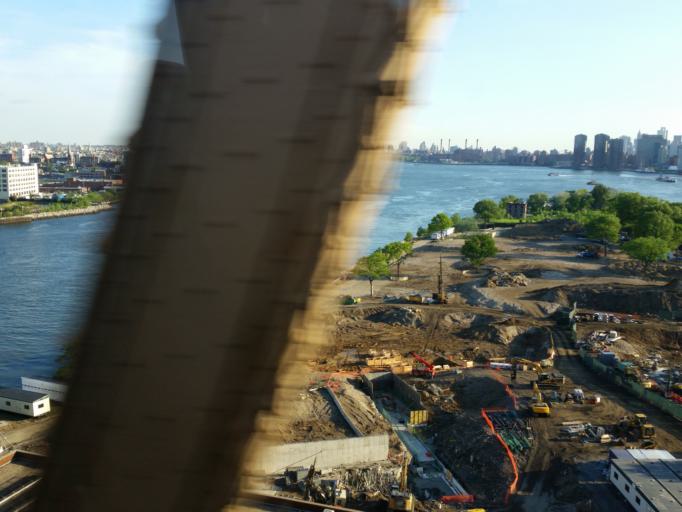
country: US
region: New York
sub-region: Queens County
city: Long Island City
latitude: 40.7568
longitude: -73.9546
